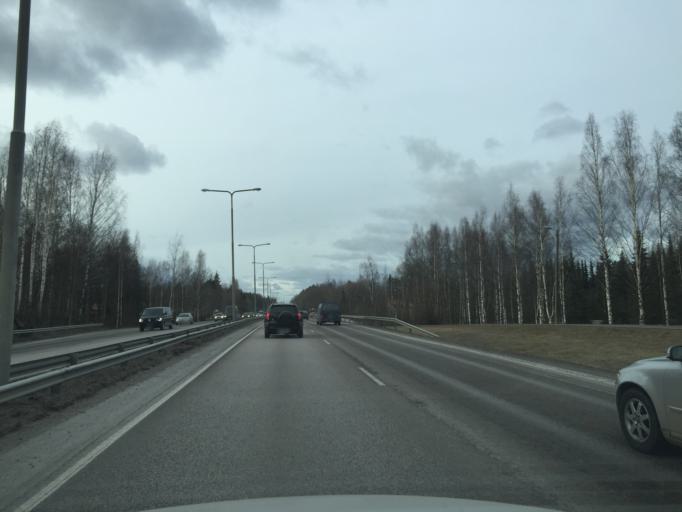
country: FI
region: Uusimaa
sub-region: Helsinki
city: Teekkarikylae
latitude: 60.2514
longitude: 24.8850
